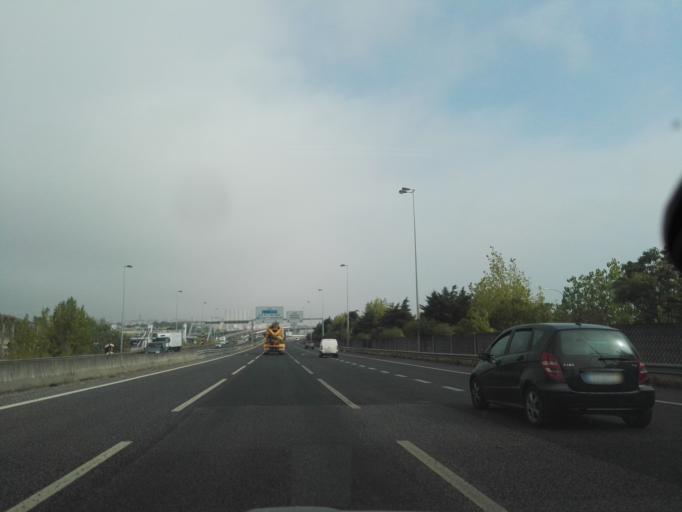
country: PT
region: Lisbon
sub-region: Loures
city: Sacavem
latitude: 38.7928
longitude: -9.0996
